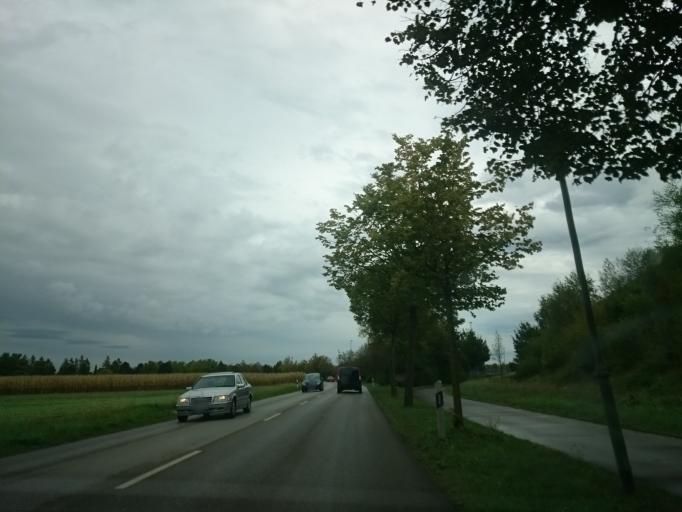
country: DE
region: Bavaria
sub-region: Swabia
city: Konigsbrunn
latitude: 48.2706
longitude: 10.8750
